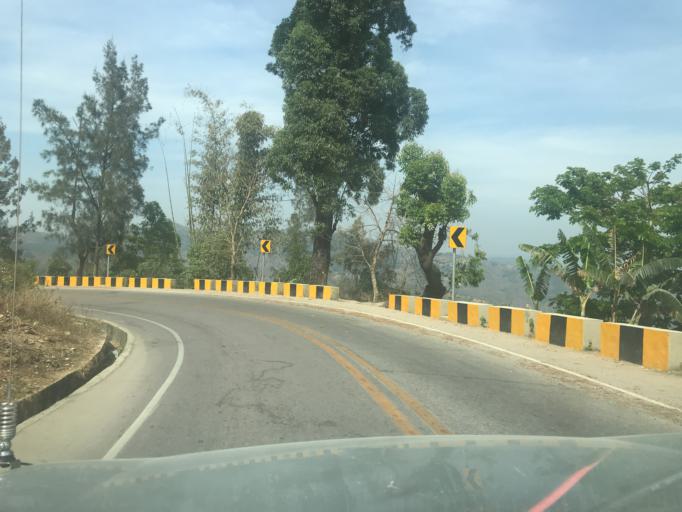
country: TL
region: Aileu
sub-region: Aileu Villa
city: Aileu
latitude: -8.6744
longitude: 125.5506
